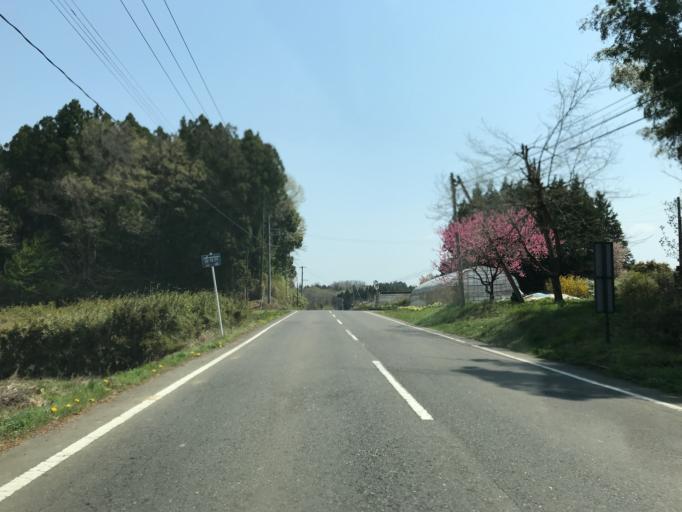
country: JP
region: Fukushima
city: Ishikawa
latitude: 37.1070
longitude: 140.3986
